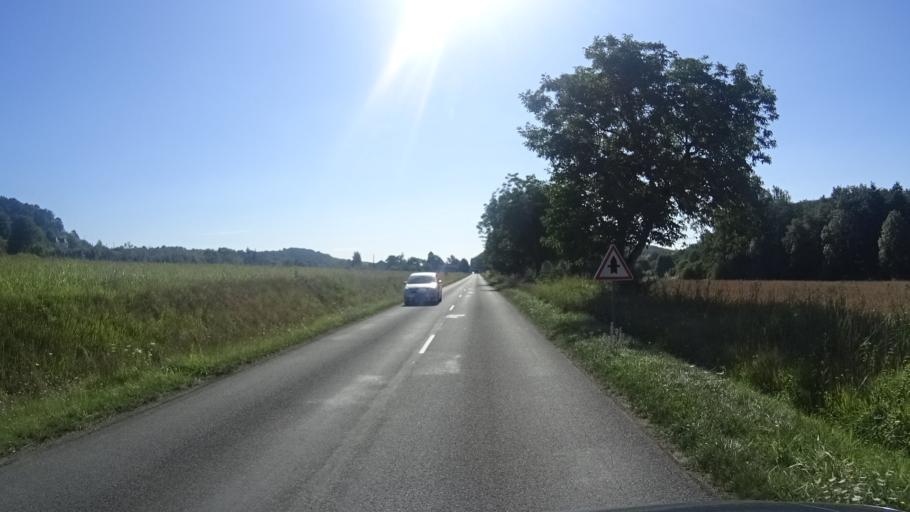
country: FR
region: Aquitaine
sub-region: Departement de la Dordogne
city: Sourzac
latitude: 45.0161
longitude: 0.4411
